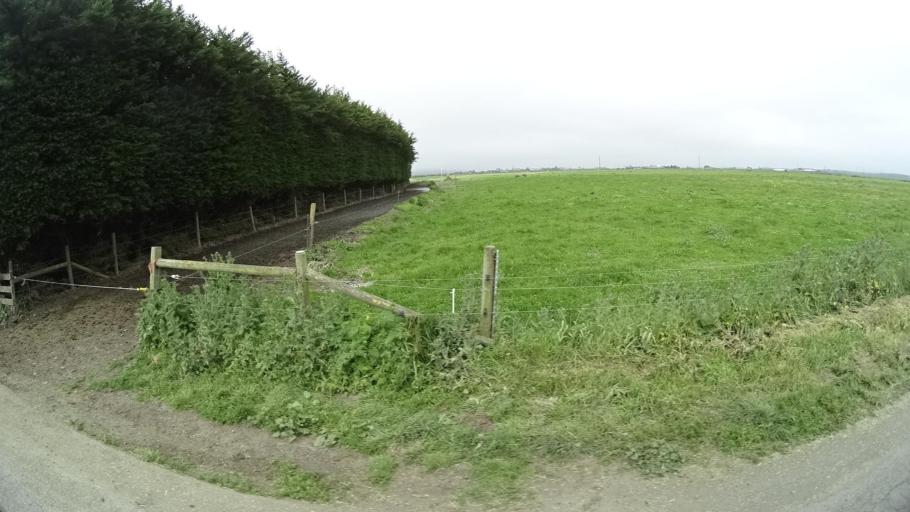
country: US
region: California
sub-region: Humboldt County
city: Fortuna
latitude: 40.5852
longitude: -124.1879
